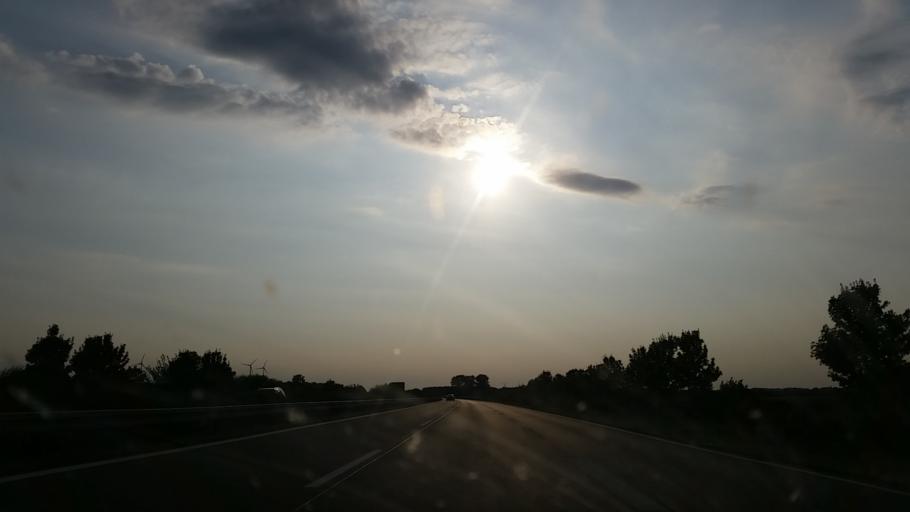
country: DE
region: Mecklenburg-Vorpommern
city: Grimmen
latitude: 54.0909
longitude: 13.0828
